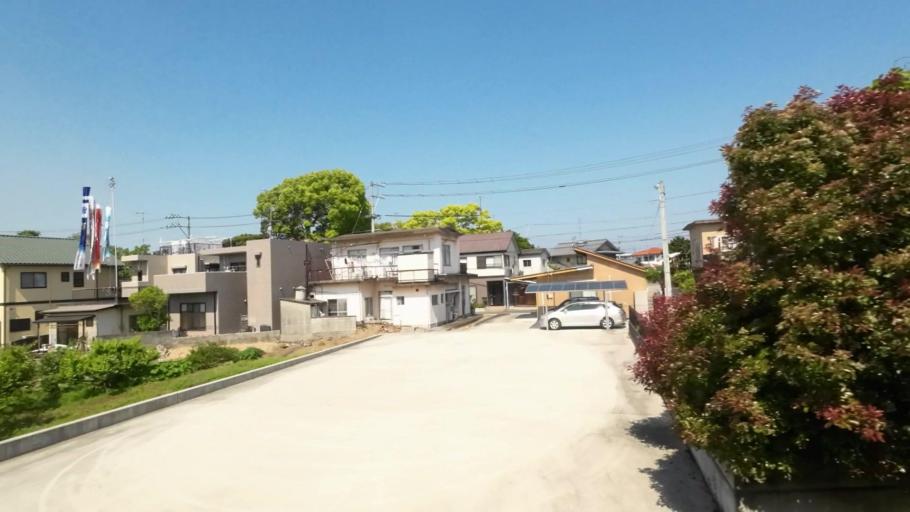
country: JP
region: Ehime
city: Kawanoecho
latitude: 34.0180
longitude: 133.5769
